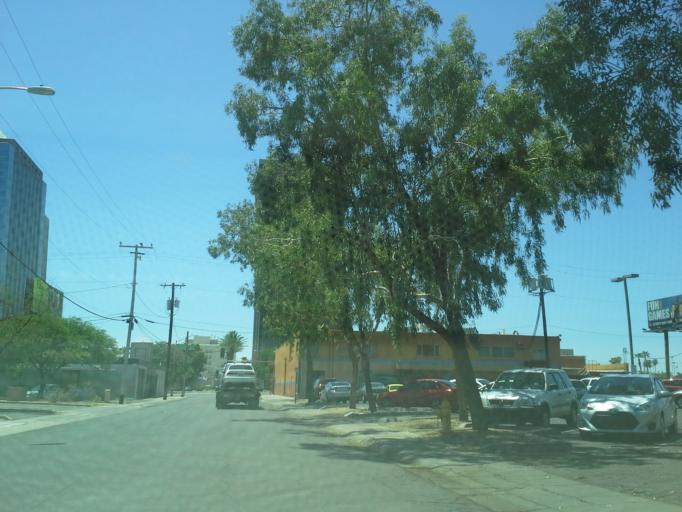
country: US
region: Arizona
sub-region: Maricopa County
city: Phoenix
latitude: 33.4924
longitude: -112.0726
